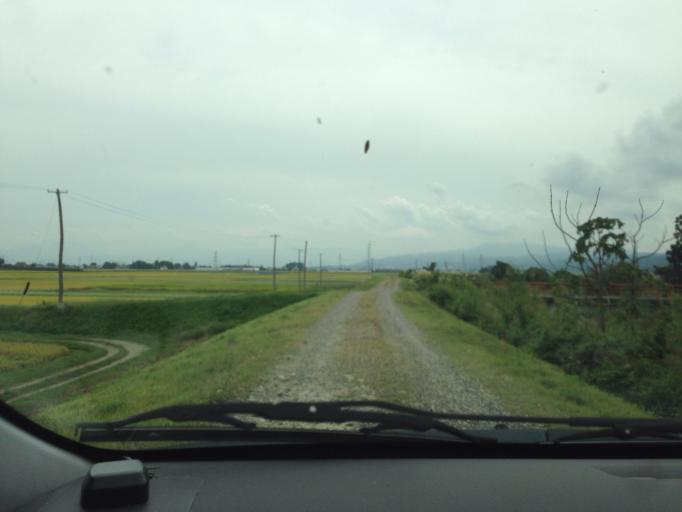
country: JP
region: Fukushima
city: Kitakata
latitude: 37.5995
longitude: 139.8229
